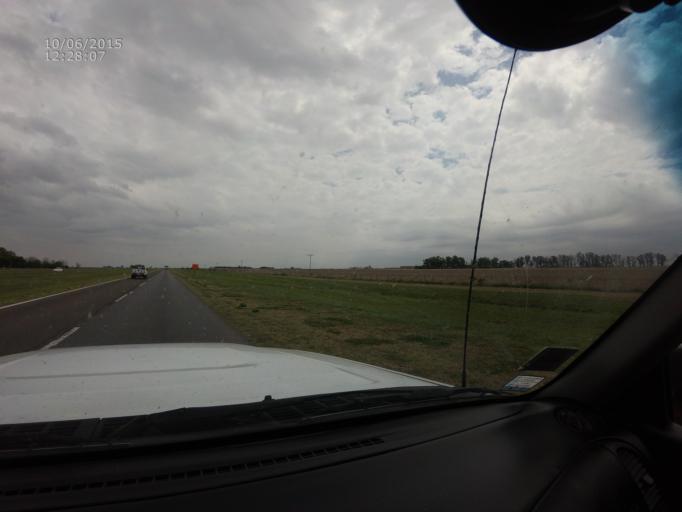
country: AR
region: Santa Fe
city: Carcarana
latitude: -32.8971
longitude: -61.0534
